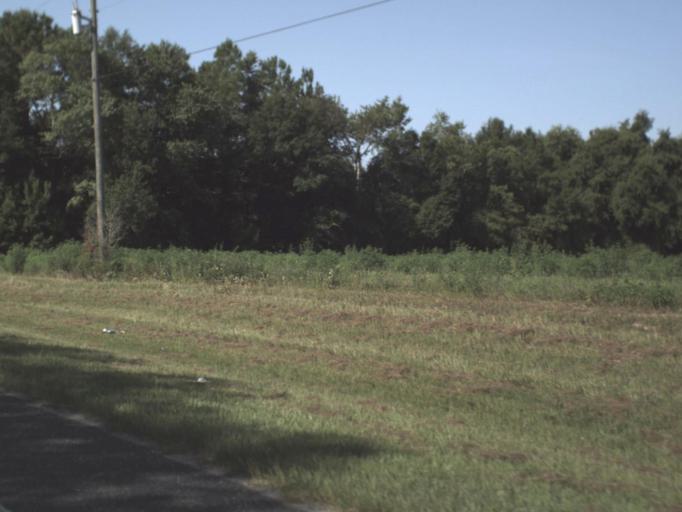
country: US
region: Florida
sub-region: Columbia County
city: Lake City
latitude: 30.0245
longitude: -82.7103
